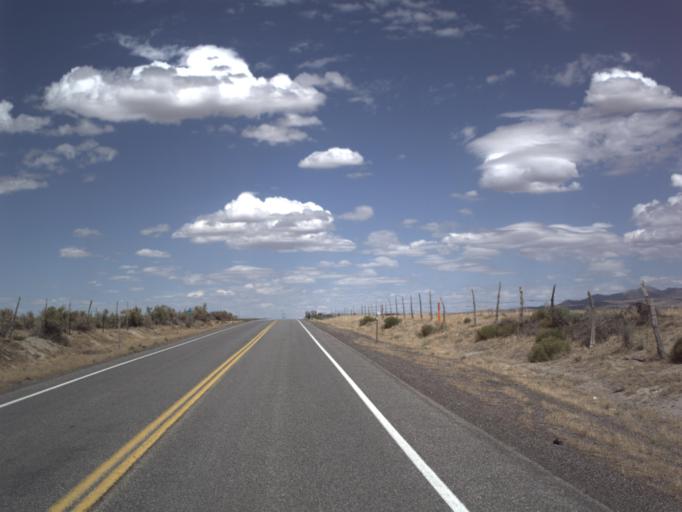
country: US
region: Utah
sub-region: Millard County
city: Fillmore
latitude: 39.1622
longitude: -112.4100
